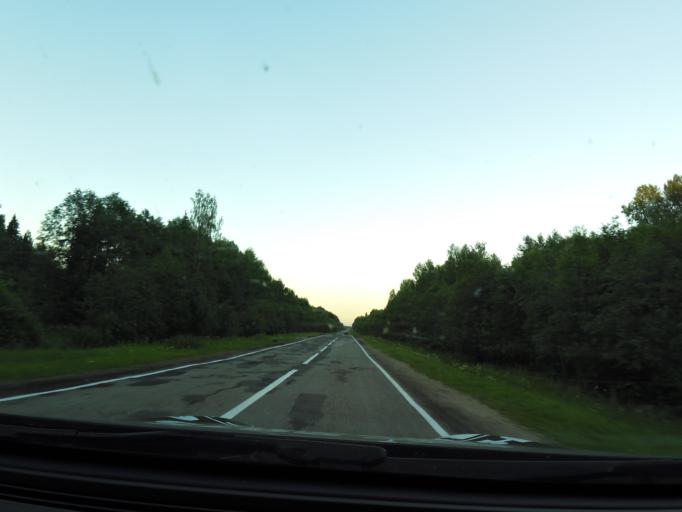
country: RU
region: Jaroslavl
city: Lyubim
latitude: 58.3577
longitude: 40.5751
